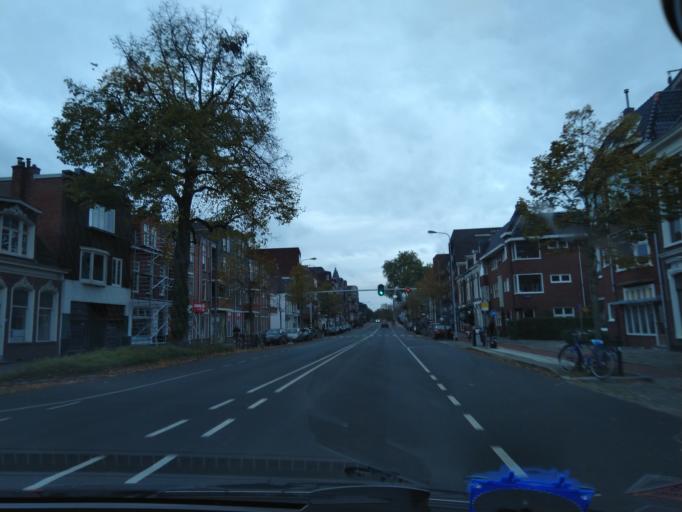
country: NL
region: Groningen
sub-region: Gemeente Groningen
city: Groningen
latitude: 53.2086
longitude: 6.5726
